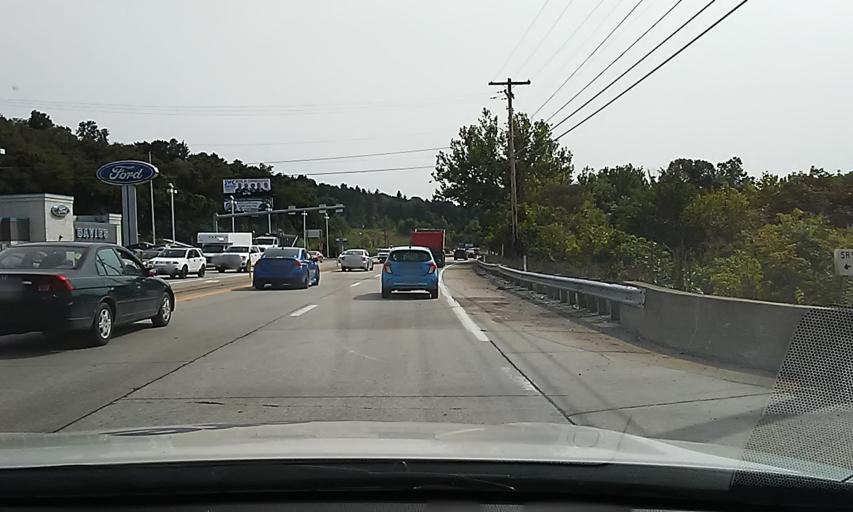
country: US
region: Pennsylvania
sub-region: Fayette County
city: Connellsville
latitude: 40.0550
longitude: -79.5619
